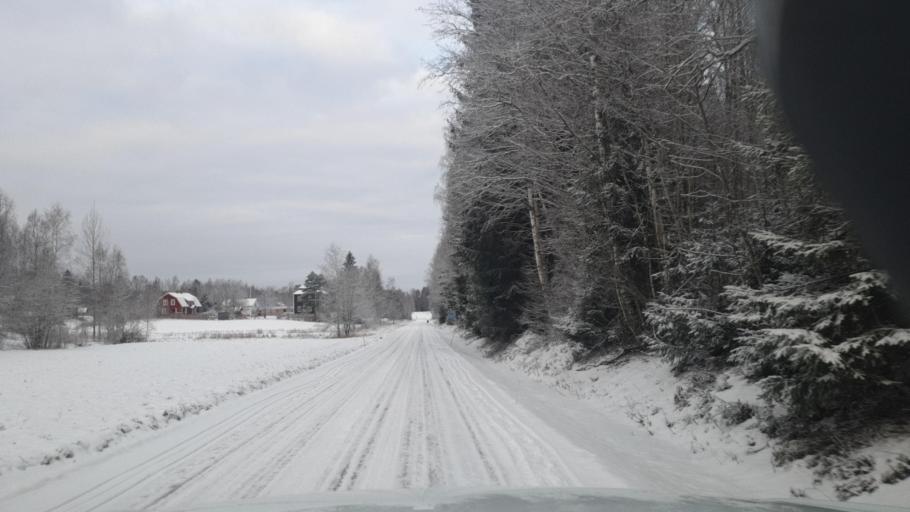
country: NO
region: Hedmark
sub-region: Eidskog
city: Skotterud
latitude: 59.8616
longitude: 11.9843
